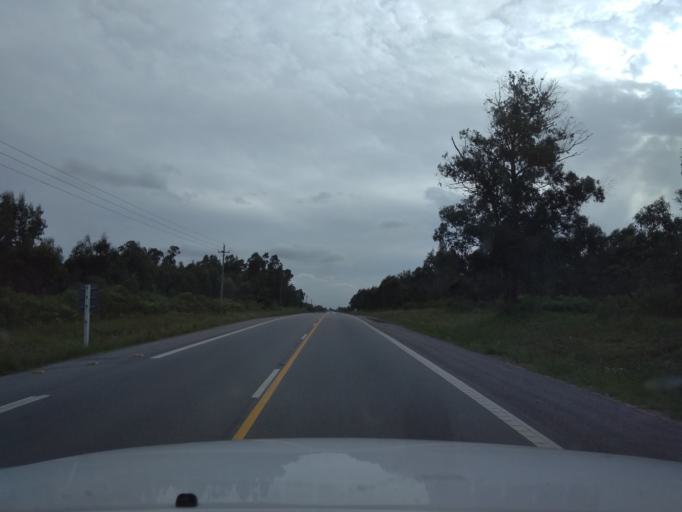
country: UY
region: Canelones
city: Joaquin Suarez
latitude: -34.6906
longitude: -56.0282
